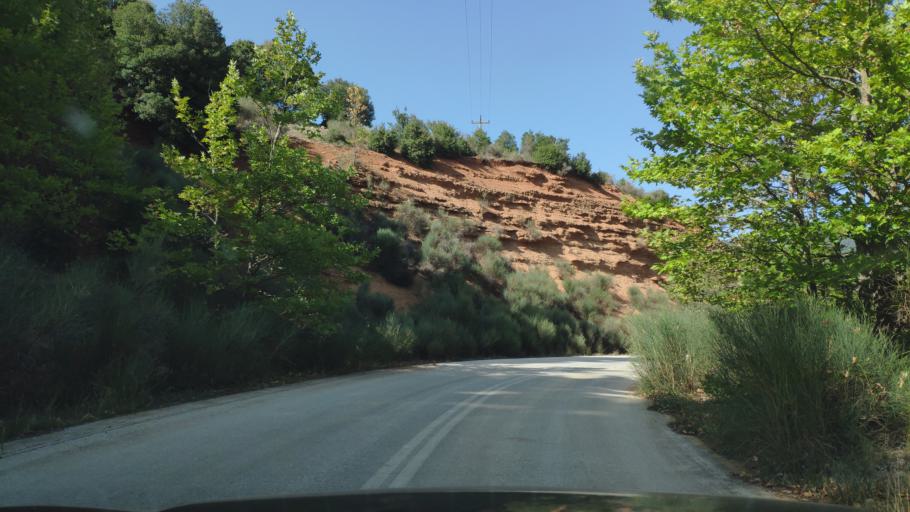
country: GR
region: West Greece
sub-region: Nomos Achaias
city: Aiyira
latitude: 37.9796
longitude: 22.3534
